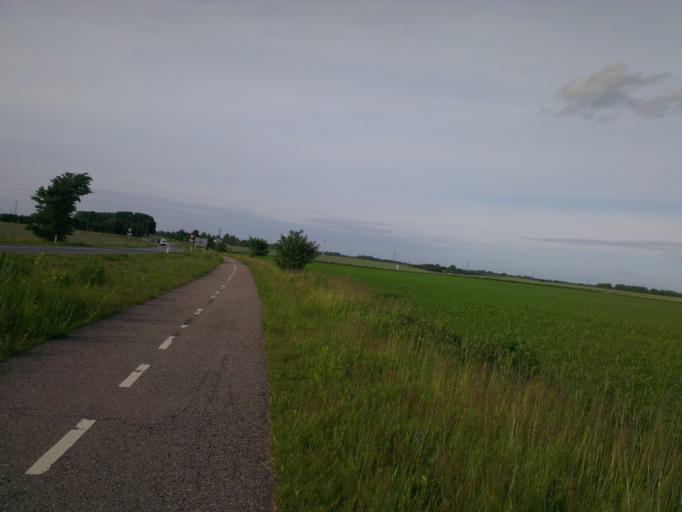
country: DK
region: Capital Region
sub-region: Frederikssund Kommune
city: Skibby
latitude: 55.7875
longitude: 11.9758
